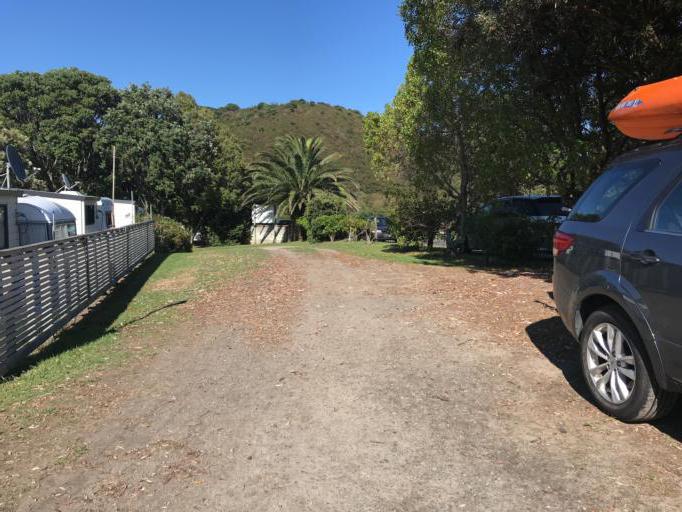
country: NZ
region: Bay of Plenty
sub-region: Western Bay of Plenty District
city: Waihi Beach
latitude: -37.4634
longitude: 175.9870
